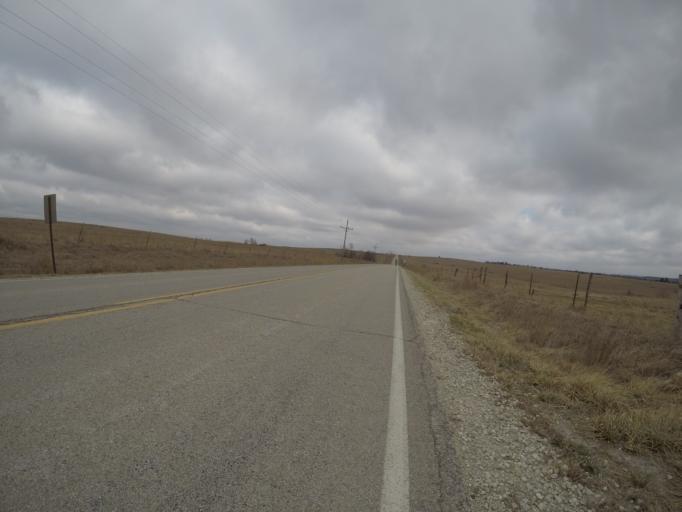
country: US
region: Kansas
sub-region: Pottawatomie County
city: Westmoreland
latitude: 39.3778
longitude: -96.4267
